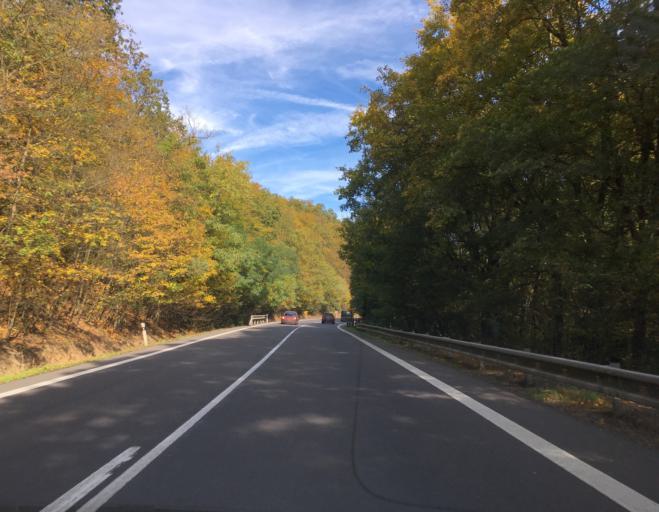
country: SK
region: Banskobystricky
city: Dudince
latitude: 48.2454
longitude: 18.9655
